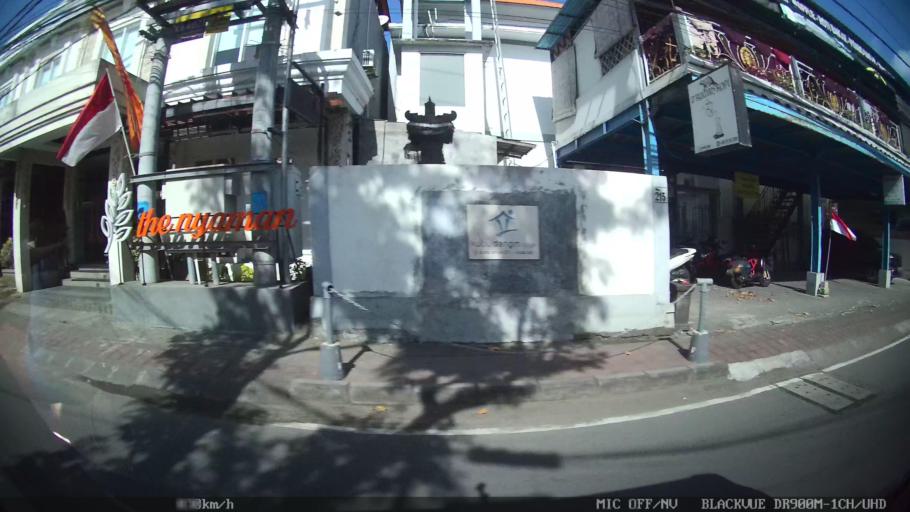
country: ID
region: Bali
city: Jabajero
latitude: -8.7285
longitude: 115.1731
